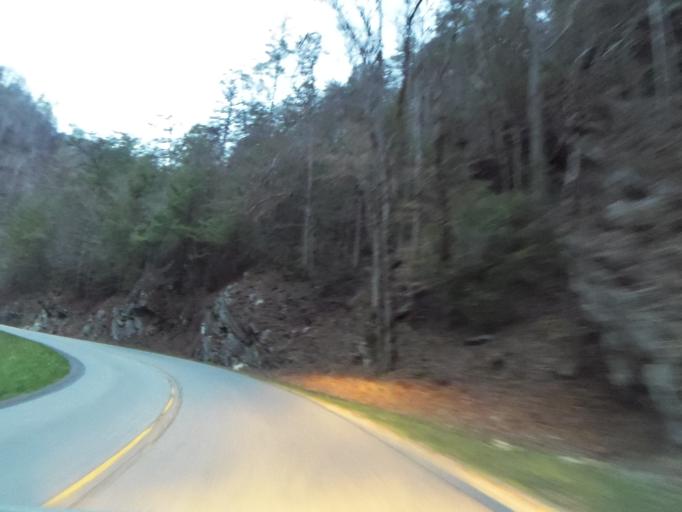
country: US
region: Tennessee
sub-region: Sevier County
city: Gatlinburg
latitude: 35.6440
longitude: -83.7148
